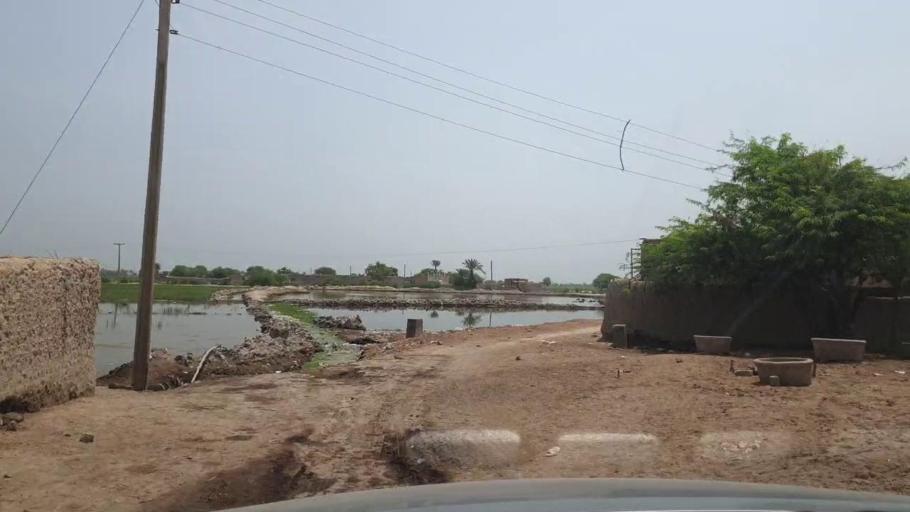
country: PK
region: Sindh
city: Garhi Yasin
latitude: 27.8706
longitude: 68.5063
